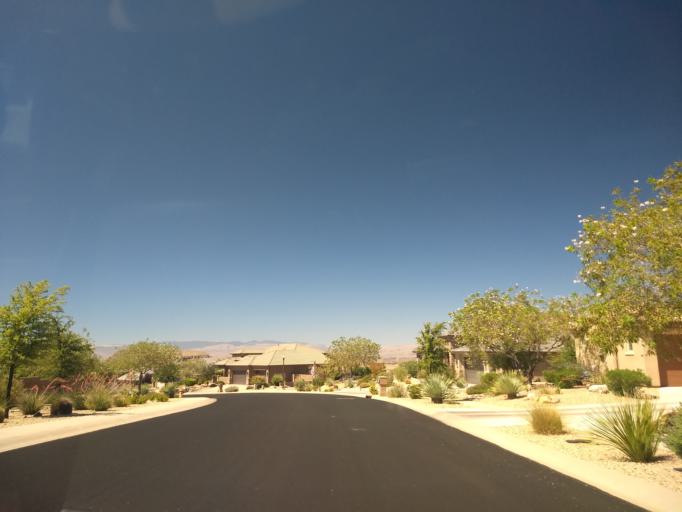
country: US
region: Utah
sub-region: Washington County
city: Washington
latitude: 37.1436
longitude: -113.4676
